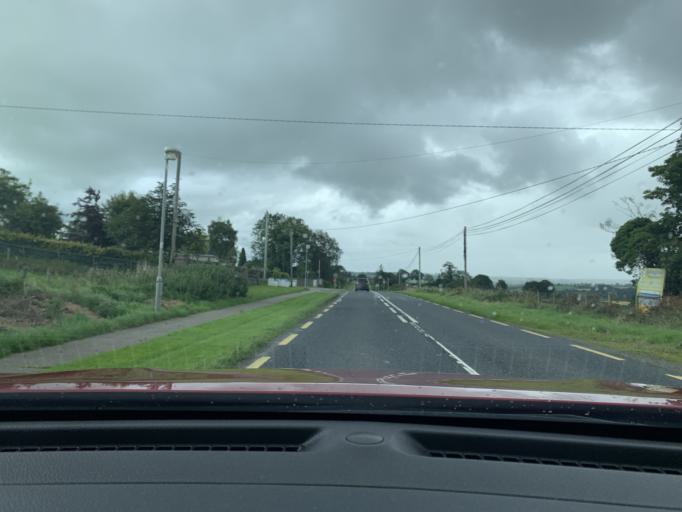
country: IE
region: Ulster
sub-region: County Donegal
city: Raphoe
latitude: 54.8002
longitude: -7.5764
